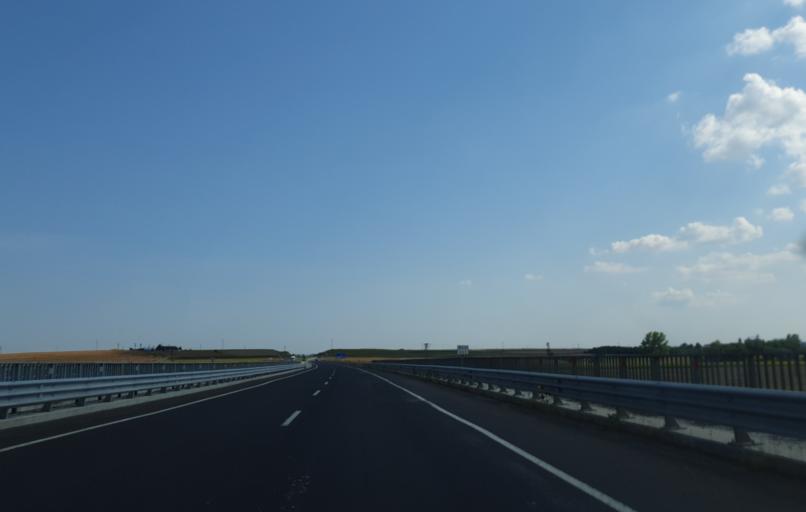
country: TR
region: Tekirdag
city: Muratli
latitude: 41.2185
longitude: 27.5325
